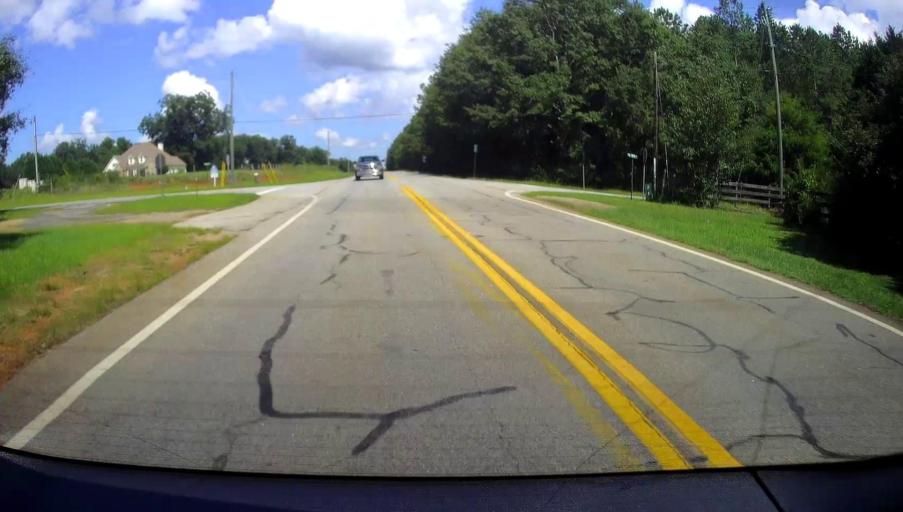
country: US
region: Georgia
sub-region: Upson County
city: Thomaston
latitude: 32.9212
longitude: -84.2322
